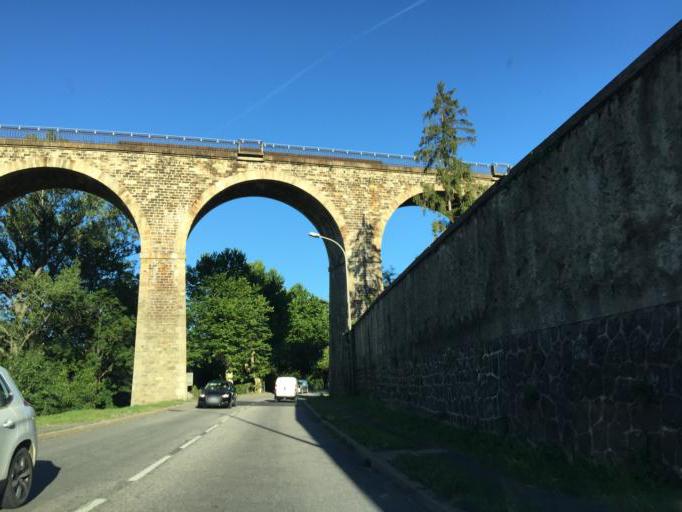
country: FR
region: Auvergne
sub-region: Departement de la Haute-Loire
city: Chadrac
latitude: 45.0563
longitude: 3.9059
